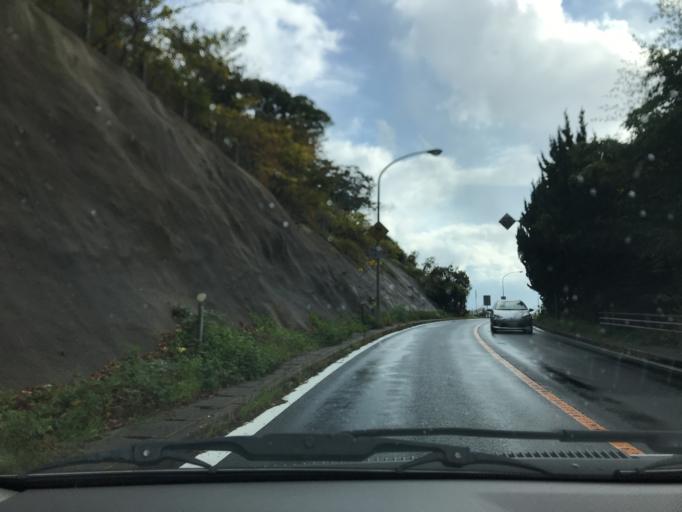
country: JP
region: Shimane
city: Sakaiminato
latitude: 35.5520
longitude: 133.2432
